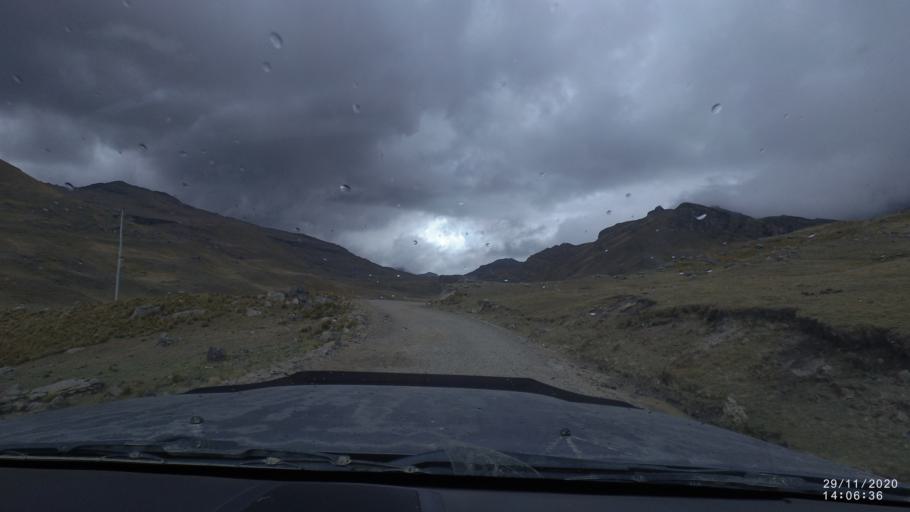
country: BO
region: Cochabamba
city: Sipe Sipe
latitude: -17.2152
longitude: -66.3789
